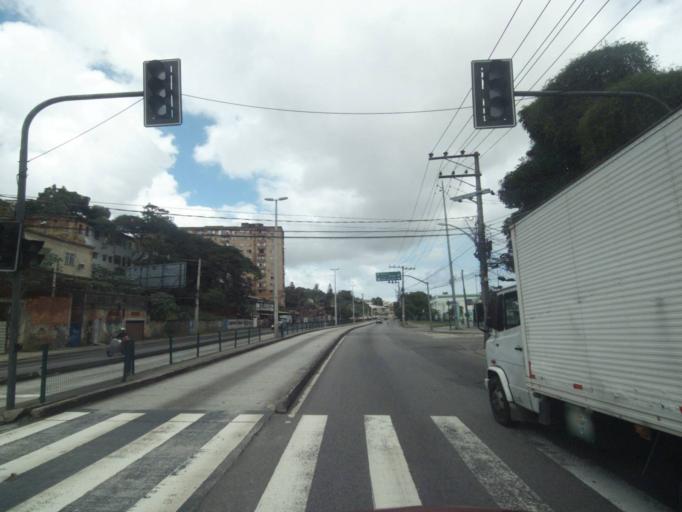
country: BR
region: Rio de Janeiro
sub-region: Sao Joao De Meriti
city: Sao Joao de Meriti
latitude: -22.9123
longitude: -43.3605
